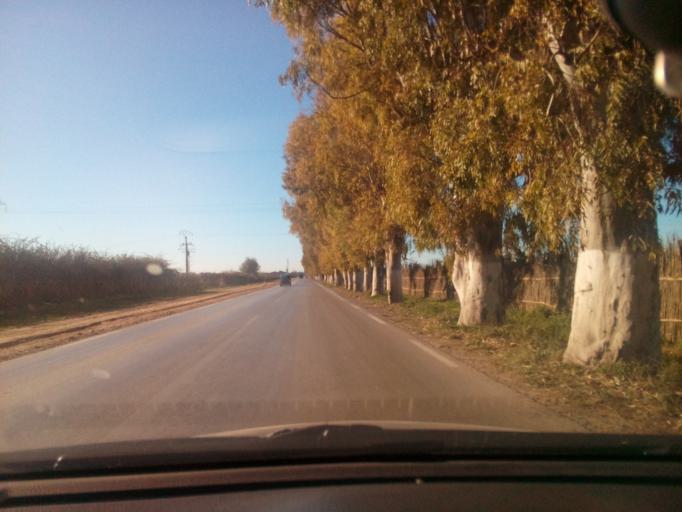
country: DZ
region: Mostaganem
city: Mostaganem
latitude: 35.8988
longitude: 0.2386
